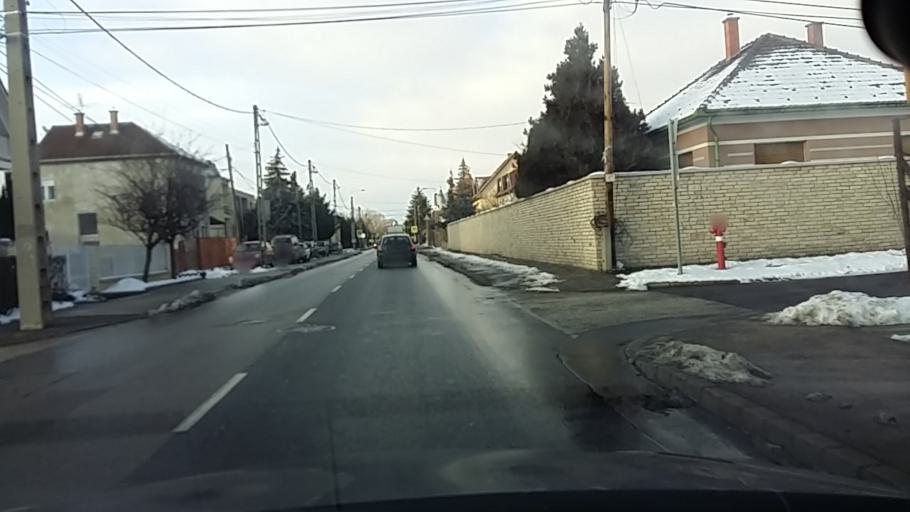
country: HU
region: Budapest
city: Budapest XVI. keruelet
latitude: 47.5272
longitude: 19.1543
